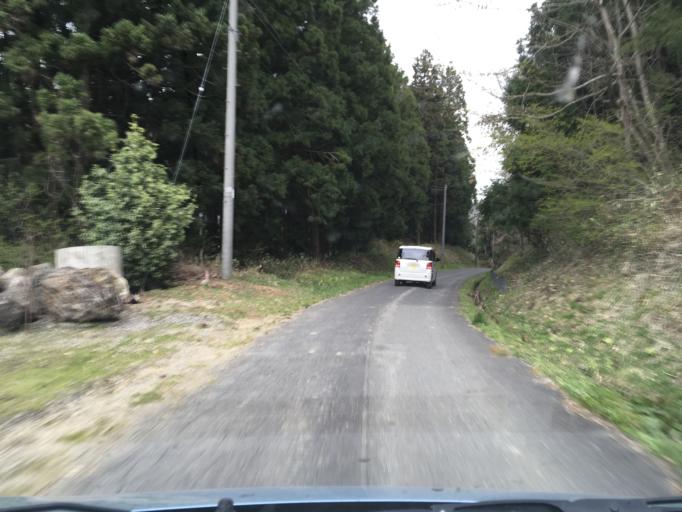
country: JP
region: Iwate
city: Ichinoseki
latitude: 38.9629
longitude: 141.2109
